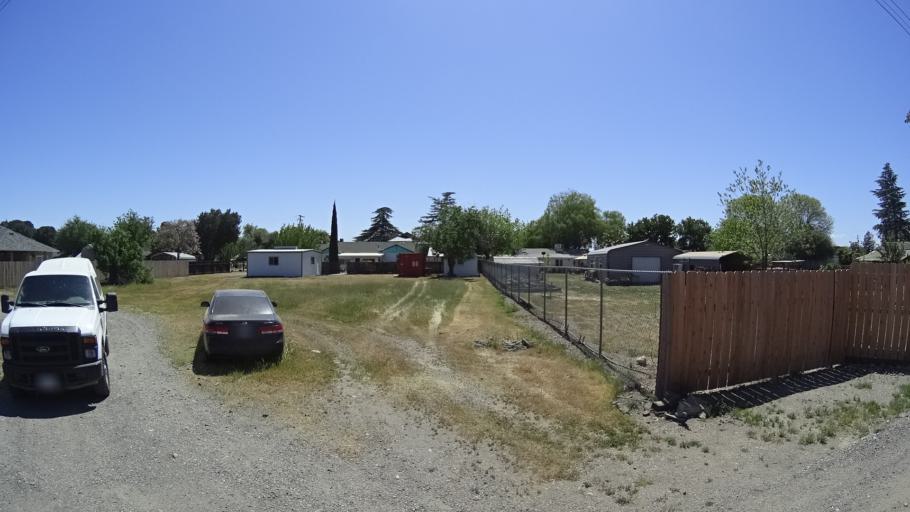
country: US
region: California
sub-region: Glenn County
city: Orland
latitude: 39.7446
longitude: -122.1812
